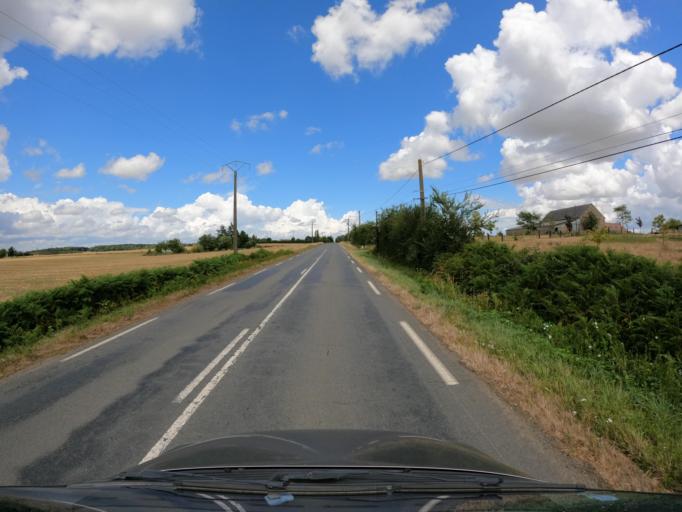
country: FR
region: Pays de la Loire
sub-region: Departement de la Sarthe
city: Juigne-sur-Sarthe
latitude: 47.8780
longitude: -0.3025
